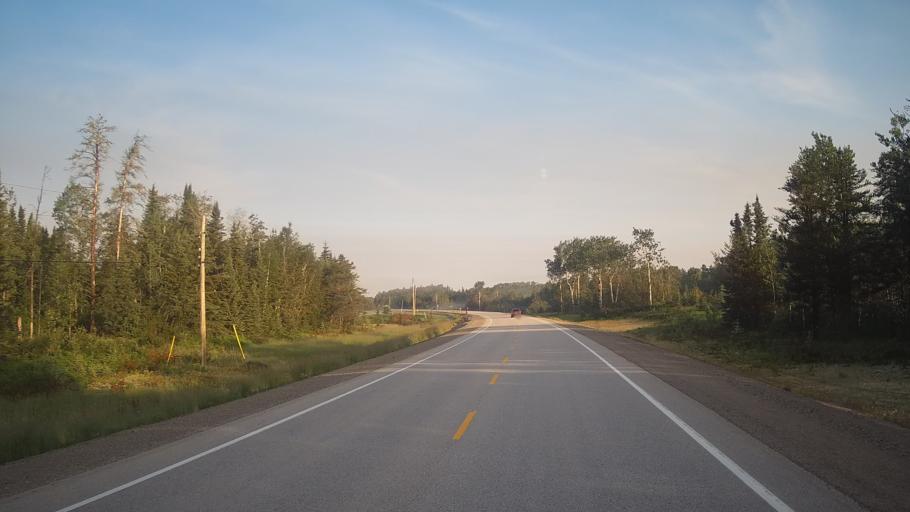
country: CA
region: Ontario
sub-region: Rainy River District
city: Atikokan
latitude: 49.2506
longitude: -91.1048
